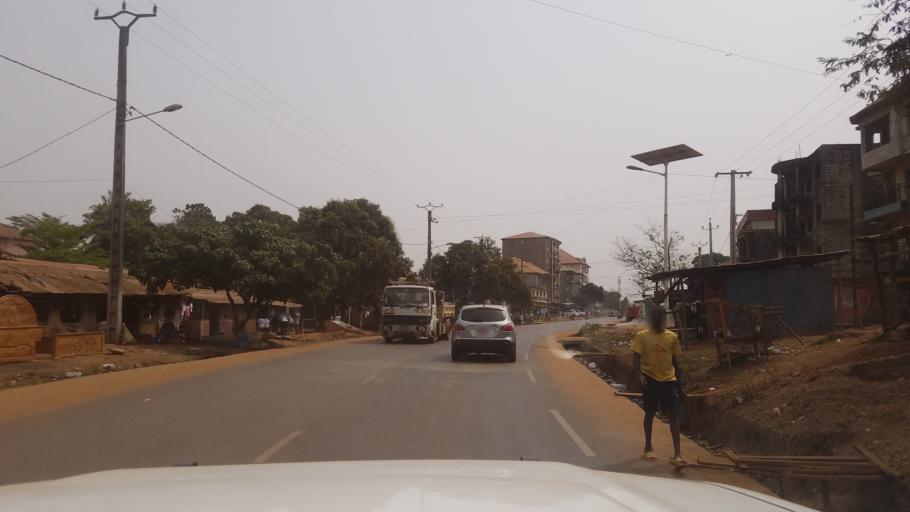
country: GN
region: Kindia
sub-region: Prefecture de Dubreka
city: Dubreka
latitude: 9.6689
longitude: -13.5903
